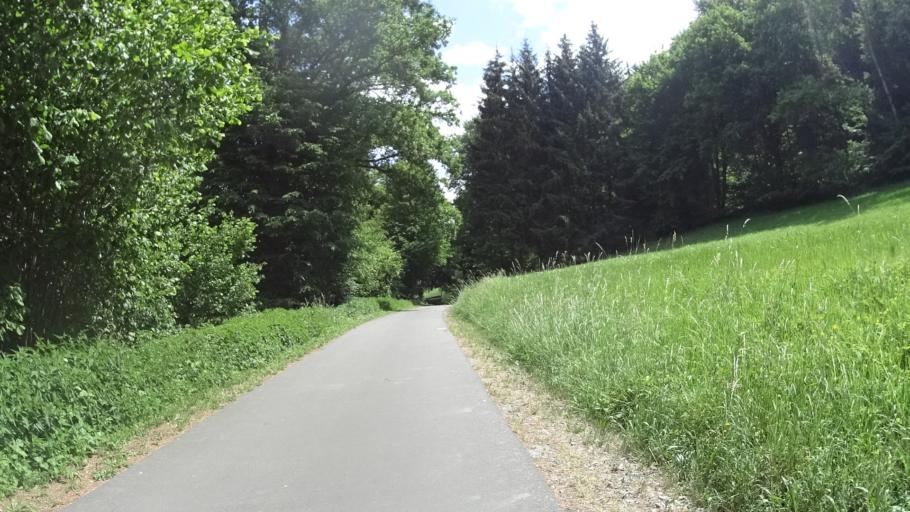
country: DE
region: Bavaria
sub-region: Regierungsbezirk Unterfranken
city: Neunkirchen
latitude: 49.6753
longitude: 9.3683
